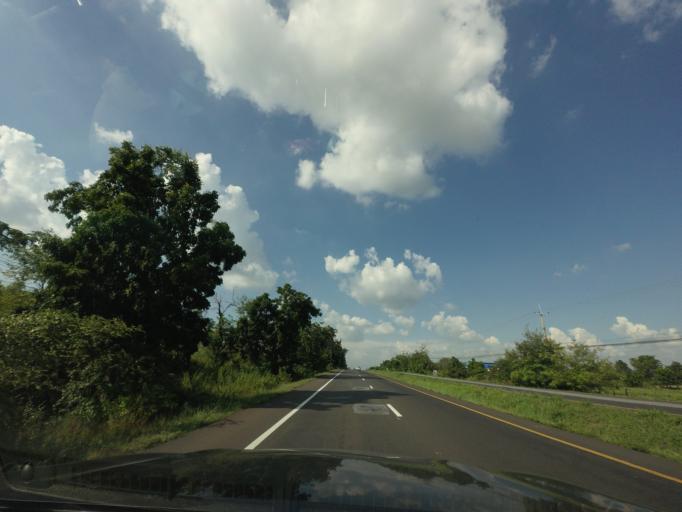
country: TH
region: Nakhon Ratchasima
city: Bua Lai
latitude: 15.6961
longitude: 102.5822
